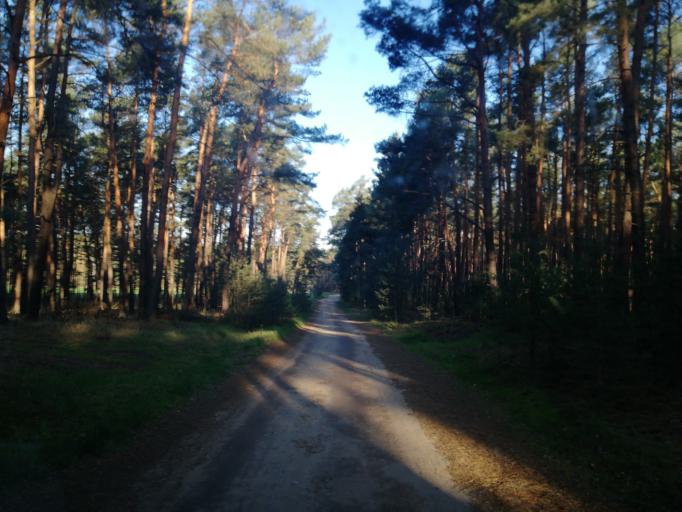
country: DE
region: Brandenburg
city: Drahnsdorf
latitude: 51.9424
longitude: 13.5734
